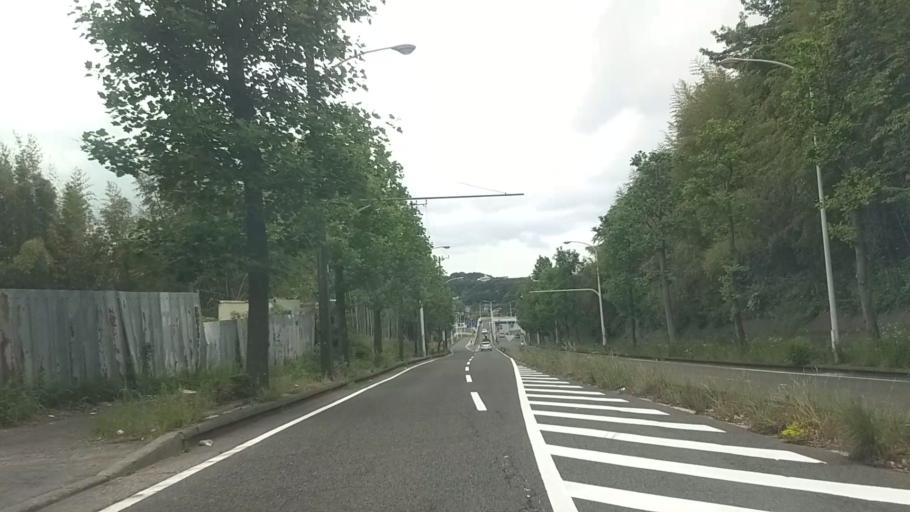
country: JP
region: Kanagawa
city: Fujisawa
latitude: 35.3628
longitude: 139.5071
